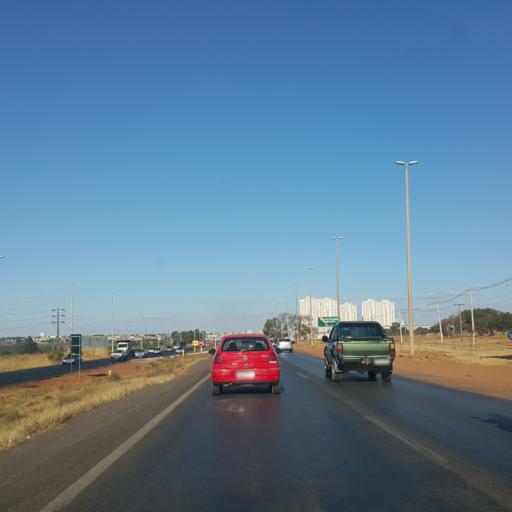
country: BR
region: Federal District
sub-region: Brasilia
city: Brasilia
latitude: -15.7924
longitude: -48.1025
